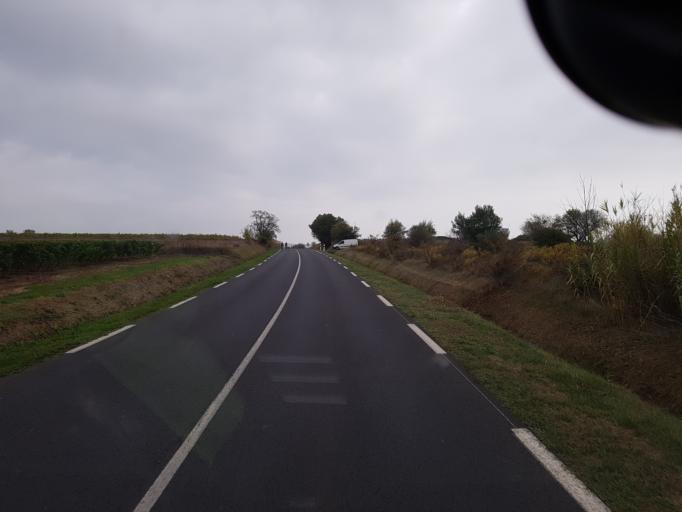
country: FR
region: Languedoc-Roussillon
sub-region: Departement de l'Herault
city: Meze
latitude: 43.4300
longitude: 3.5644
